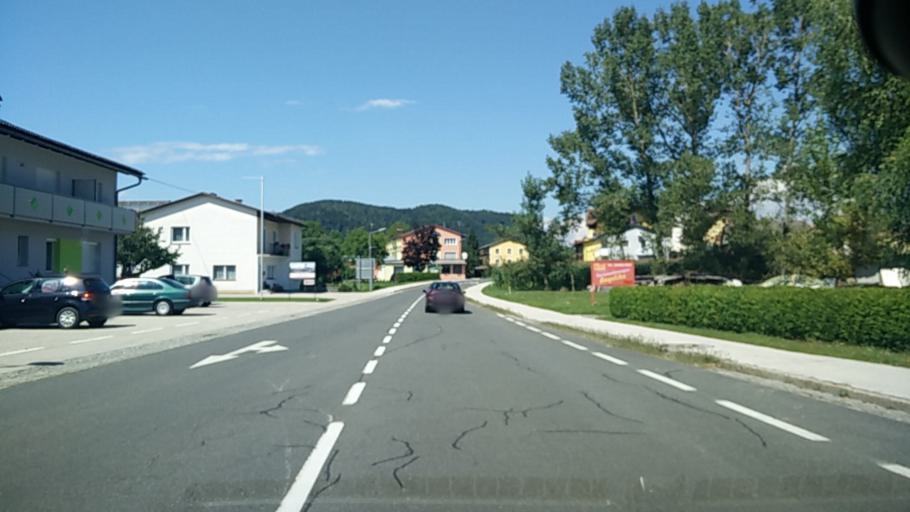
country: AT
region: Carinthia
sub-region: Politischer Bezirk Volkermarkt
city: Sittersdorf
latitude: 46.5774
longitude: 14.5642
